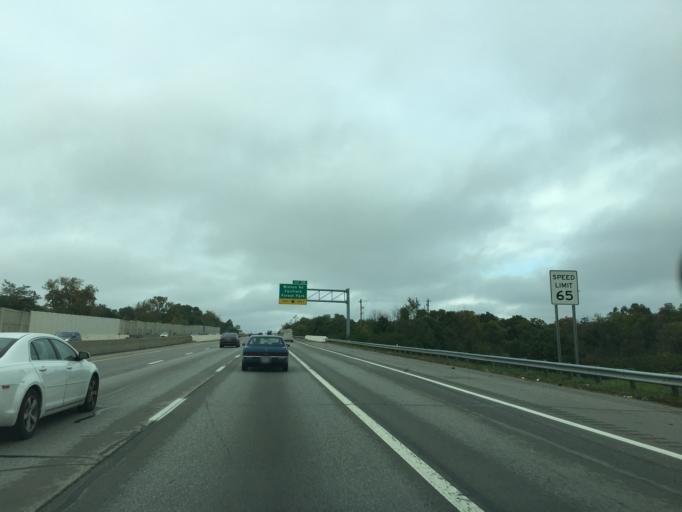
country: US
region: Ohio
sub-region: Hamilton County
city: Forest Park
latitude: 39.2976
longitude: -84.5016
